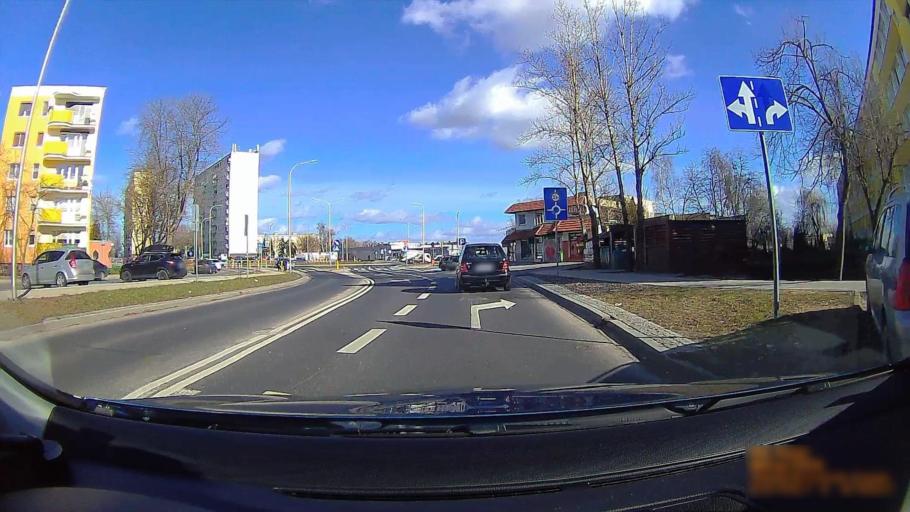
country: PL
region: Greater Poland Voivodeship
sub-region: Konin
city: Konin
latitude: 52.2315
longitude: 18.2762
